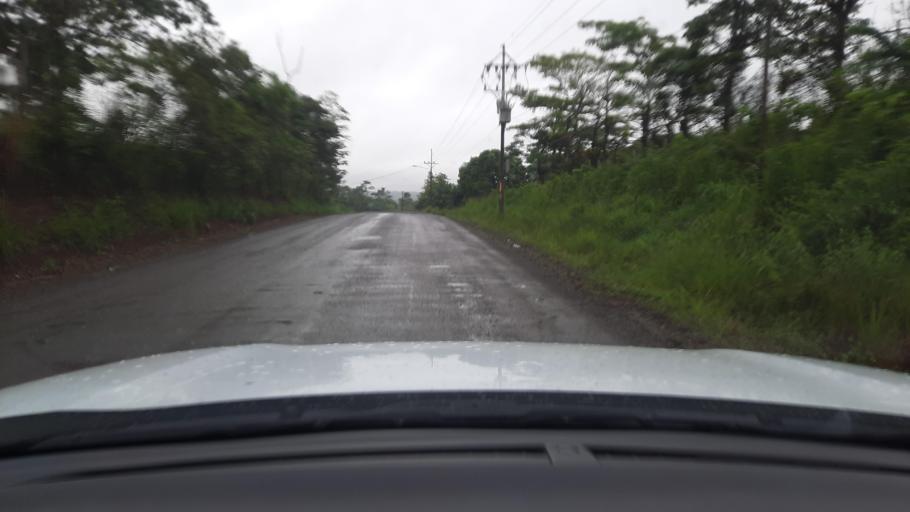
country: NI
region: Rivas
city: Cardenas
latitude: 11.0287
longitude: -85.3645
